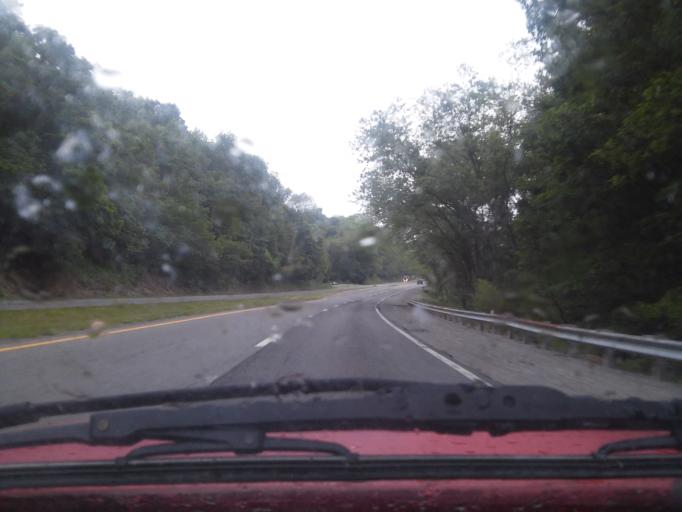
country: US
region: Virginia
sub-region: Montgomery County
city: Prices Fork
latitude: 37.3051
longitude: -80.5090
